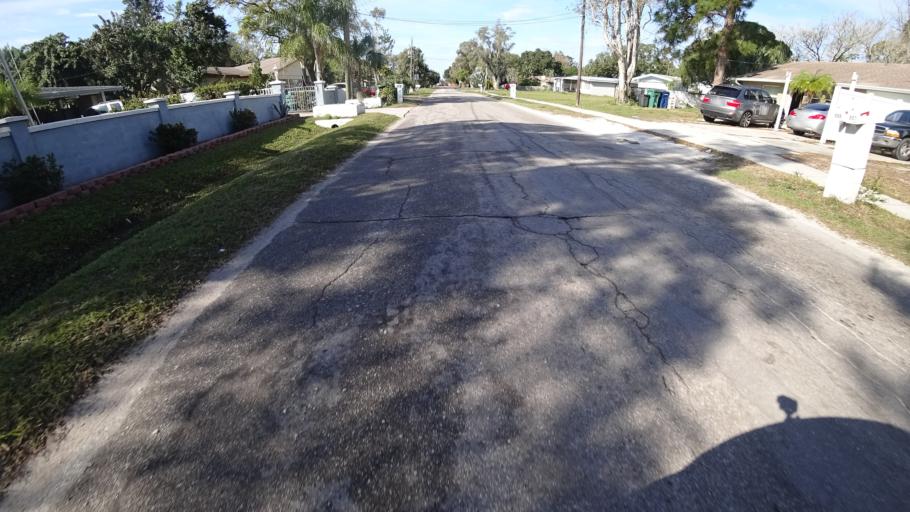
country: US
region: Florida
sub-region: Manatee County
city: Bayshore Gardens
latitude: 27.4349
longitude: -82.5709
